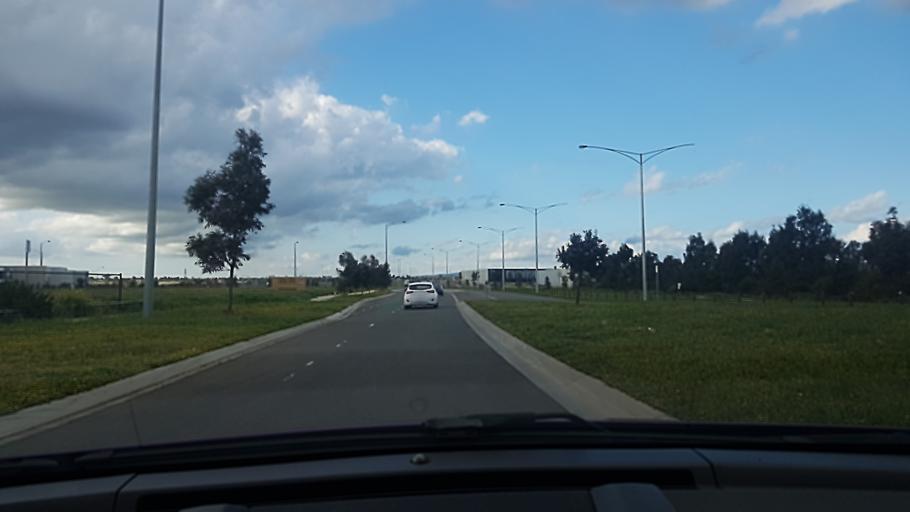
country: AU
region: Victoria
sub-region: Whittlesea
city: Lalor
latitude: -37.6468
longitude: 145.0059
